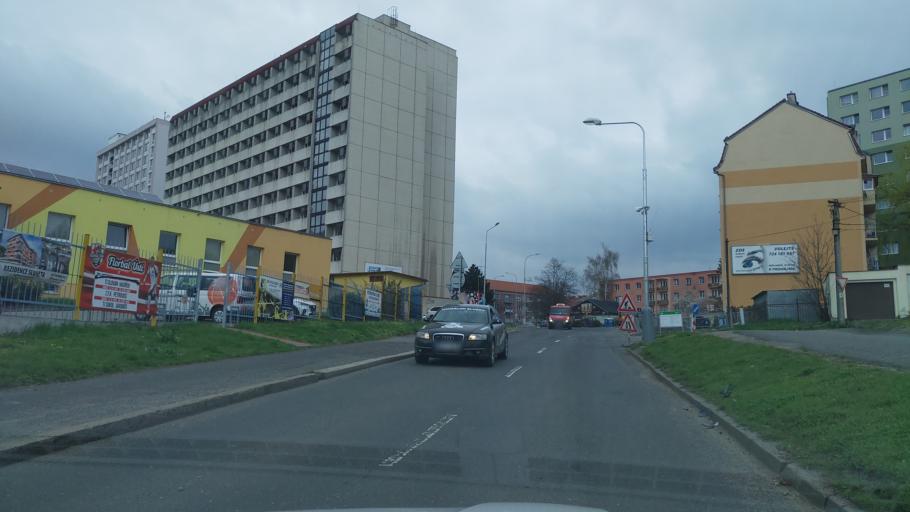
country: CZ
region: Ustecky
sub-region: Okres Usti nad Labem
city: Usti nad Labem
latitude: 50.6646
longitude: 14.0129
